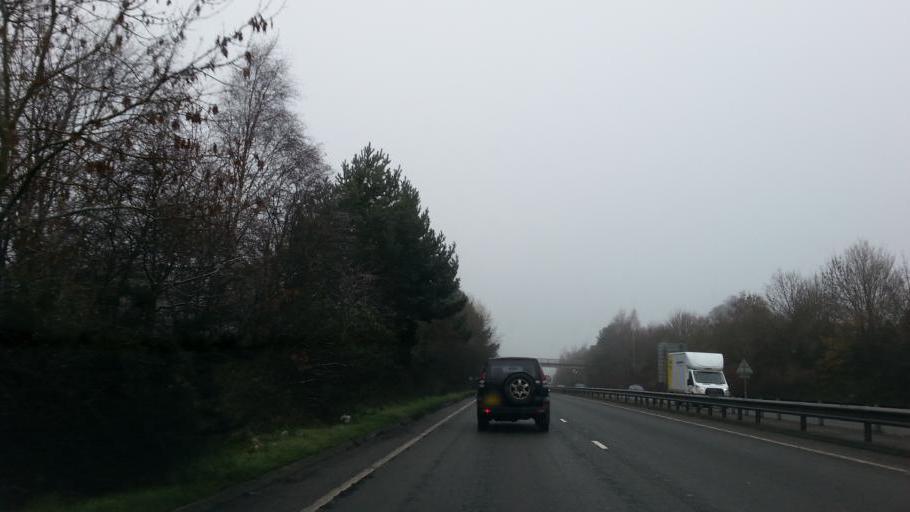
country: GB
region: England
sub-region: Cheshire East
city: Wilmslow
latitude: 53.3221
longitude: -2.2265
